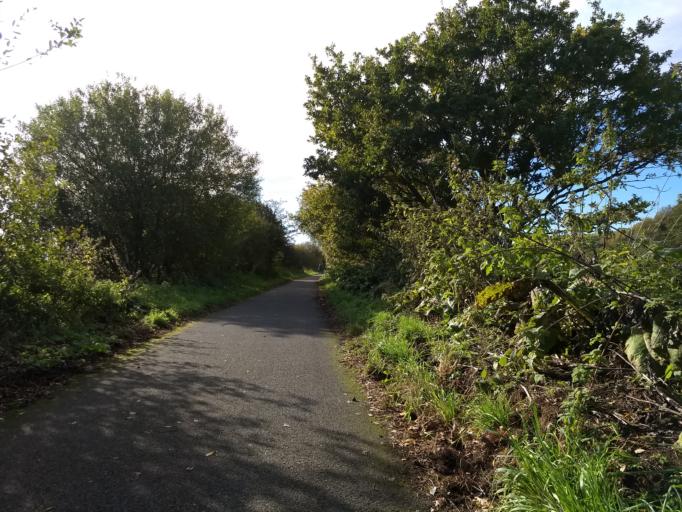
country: GB
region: England
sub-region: Isle of Wight
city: Newchurch
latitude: 50.6610
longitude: -1.2388
